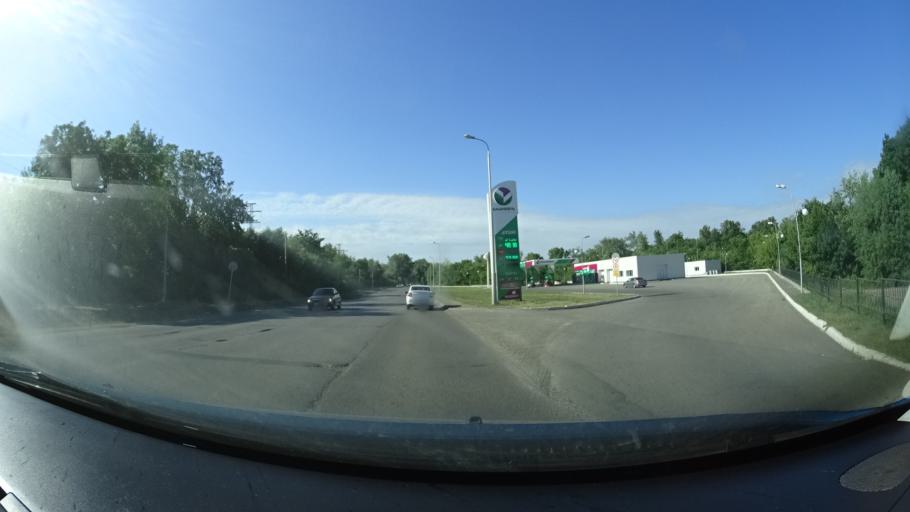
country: RU
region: Bashkortostan
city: Ufa
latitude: 54.8472
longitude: 56.0766
